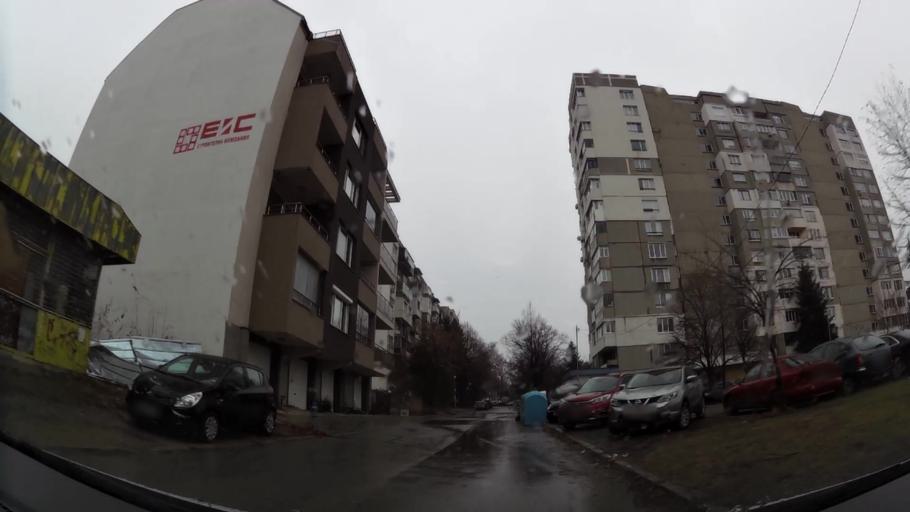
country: BG
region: Sofia-Capital
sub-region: Stolichna Obshtina
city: Sofia
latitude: 42.6504
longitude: 23.3708
